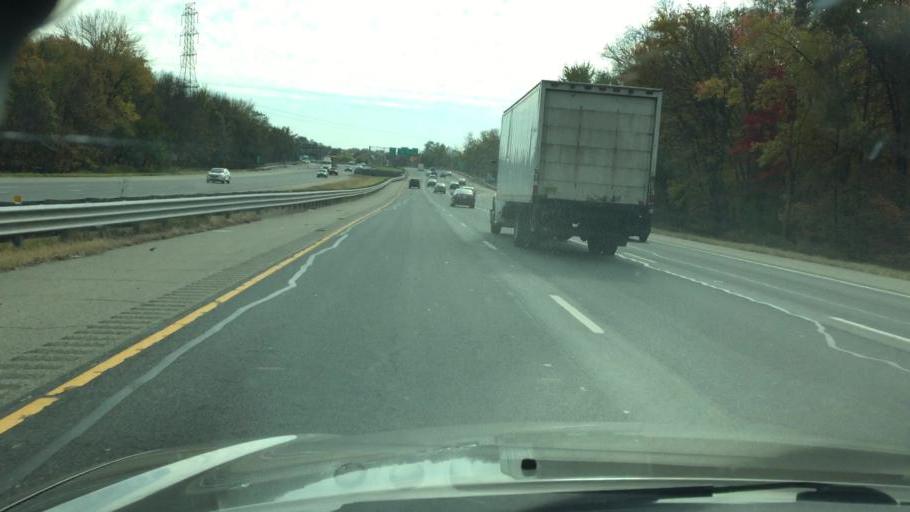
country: US
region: New Jersey
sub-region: Union County
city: Summit
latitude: 40.7448
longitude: -74.3712
